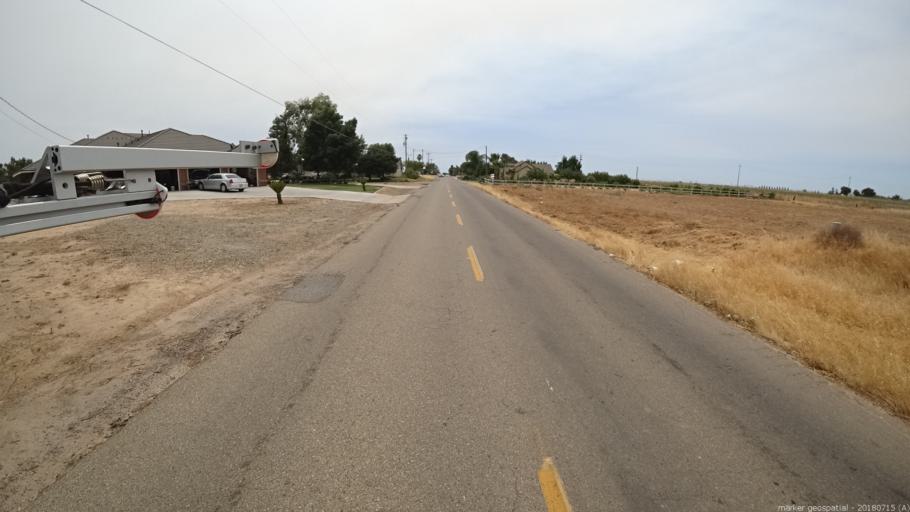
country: US
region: California
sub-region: Madera County
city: Madera Acres
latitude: 36.9983
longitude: -120.0915
